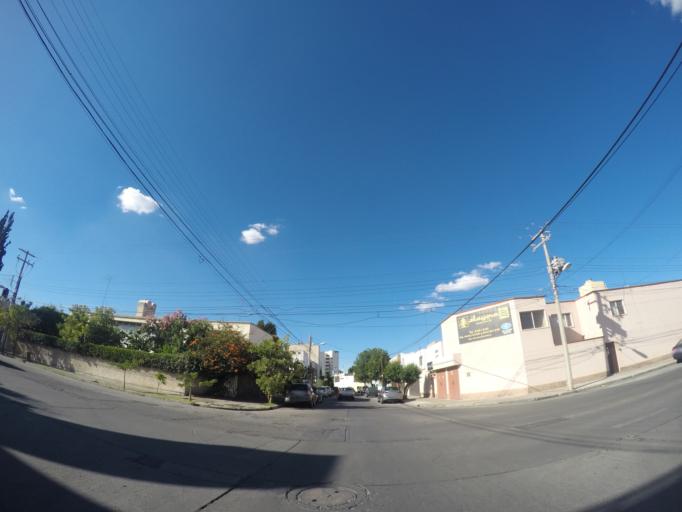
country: MX
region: San Luis Potosi
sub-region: San Luis Potosi
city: San Luis Potosi
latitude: 22.1467
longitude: -101.0021
